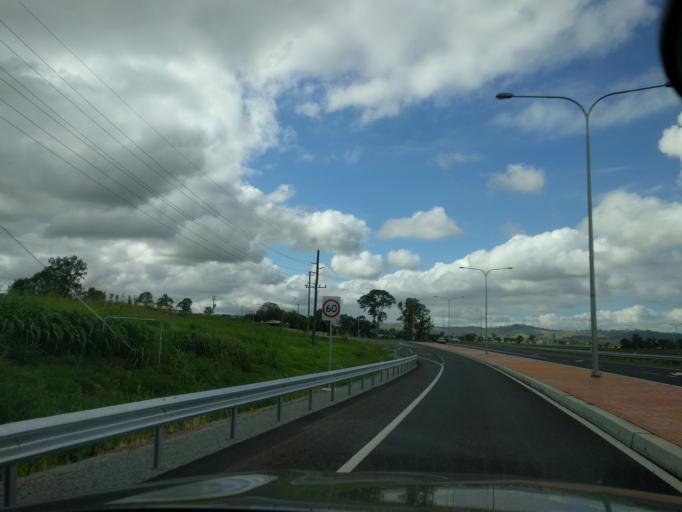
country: AU
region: Queensland
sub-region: Logan
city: Cedar Vale
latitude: -27.9879
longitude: 152.9882
